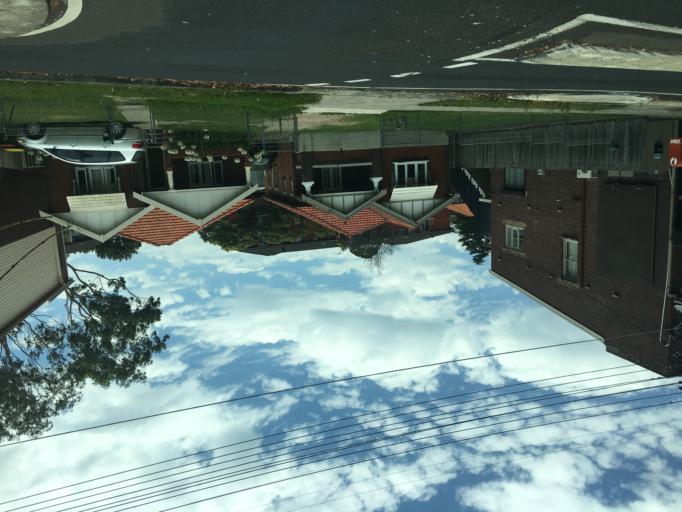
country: AU
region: New South Wales
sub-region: Hunters Hill
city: Gladesville
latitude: -33.8286
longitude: 151.1295
